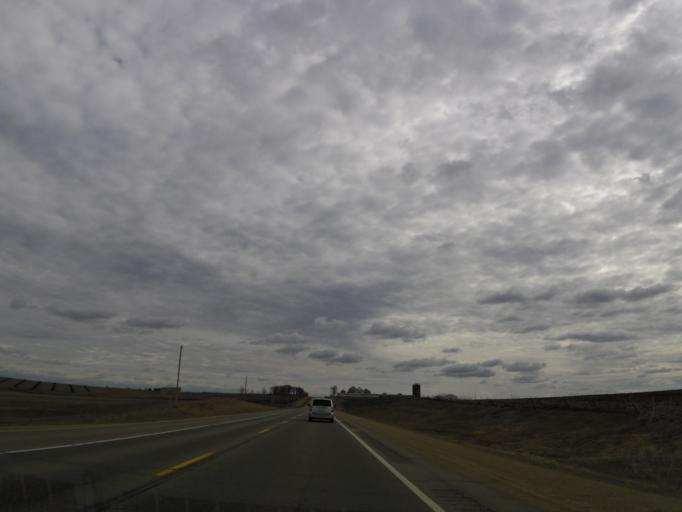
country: US
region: Iowa
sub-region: Chickasaw County
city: New Hampton
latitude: 43.1840
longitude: -92.2985
